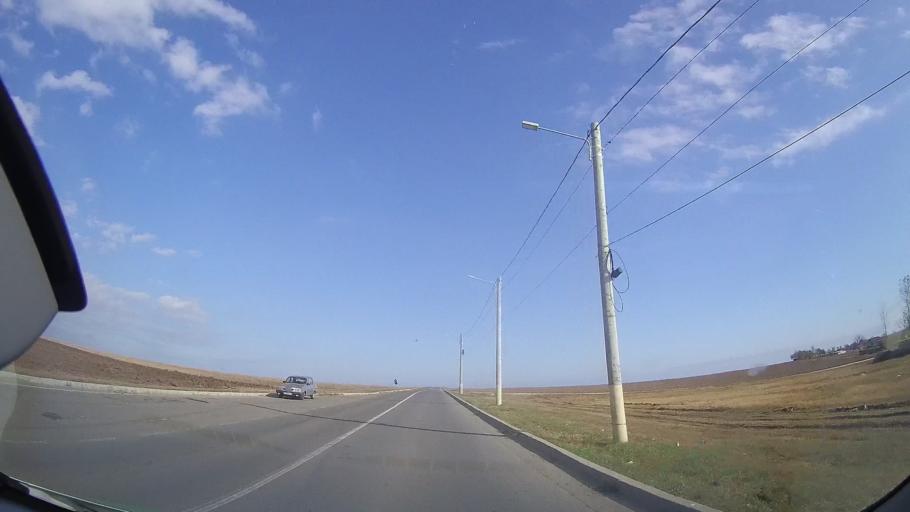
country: RO
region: Constanta
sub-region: Comuna Douazeci si Trei August
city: Dulcesti
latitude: 43.9120
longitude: 28.5521
